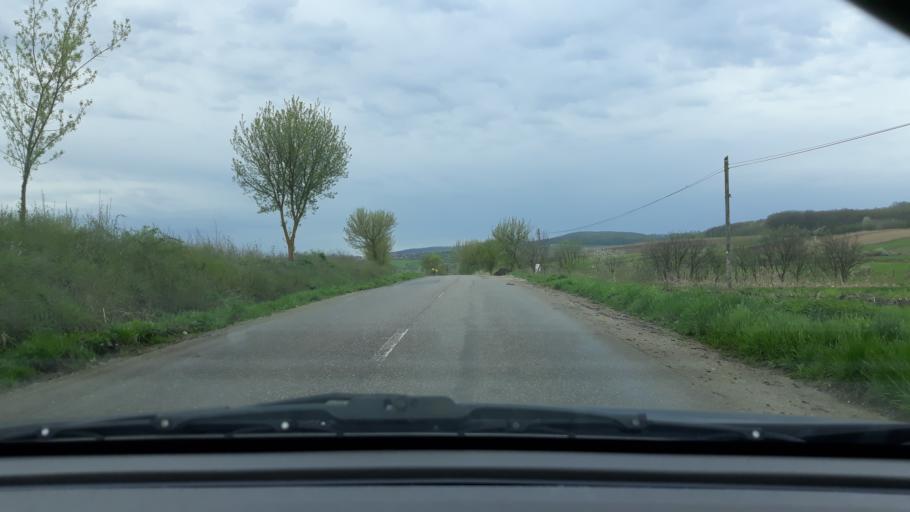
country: RO
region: Salaj
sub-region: Comuna Salatig
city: Salatig
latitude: 47.3790
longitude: 23.1444
